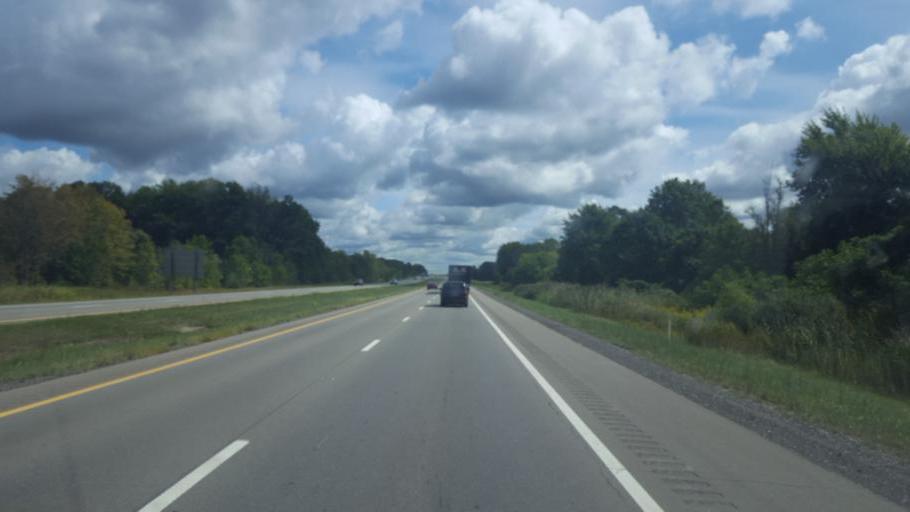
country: US
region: Ohio
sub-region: Lorain County
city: Elyria
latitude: 41.3232
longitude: -82.0970
